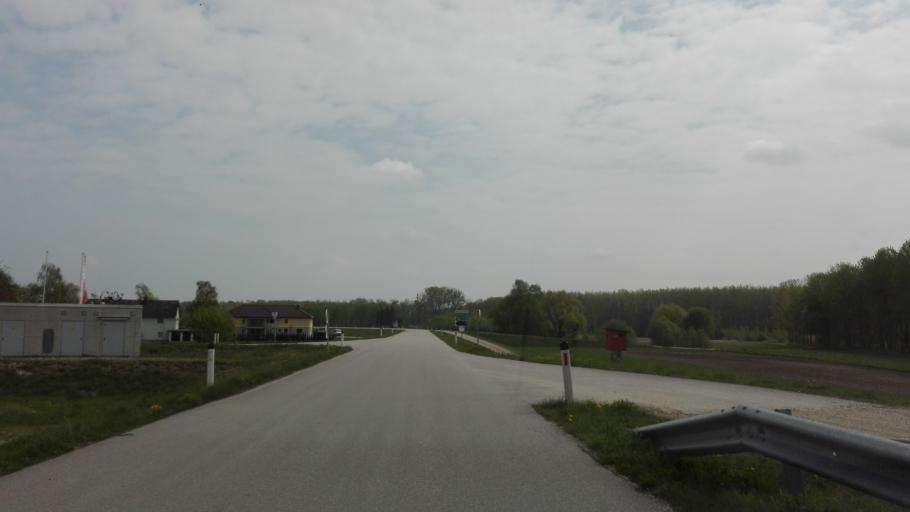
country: AT
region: Lower Austria
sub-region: Politischer Bezirk Amstetten
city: Strengberg
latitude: 48.1822
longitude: 14.6484
